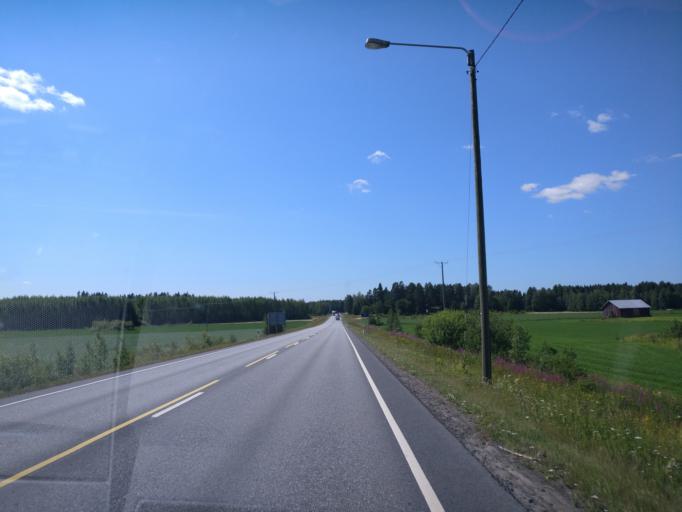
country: FI
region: Satakunta
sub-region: Pori
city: Kullaa
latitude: 61.4629
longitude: 22.1524
